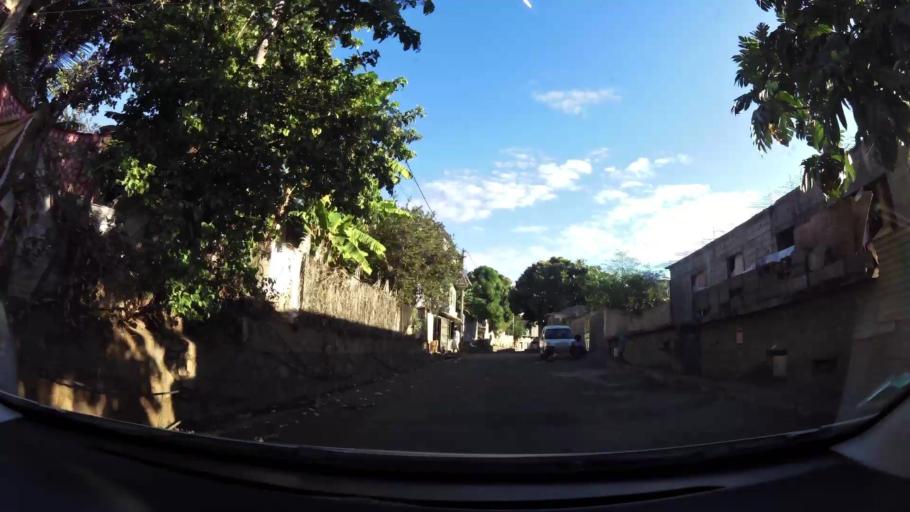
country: YT
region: Koungou
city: Koungou
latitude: -12.7334
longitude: 45.2061
